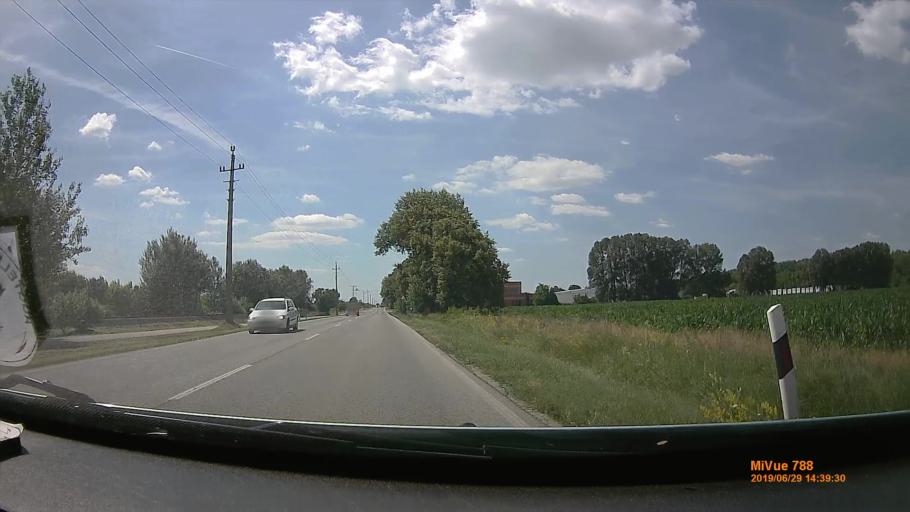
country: HU
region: Komarom-Esztergom
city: Tat
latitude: 47.7537
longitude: 18.6036
